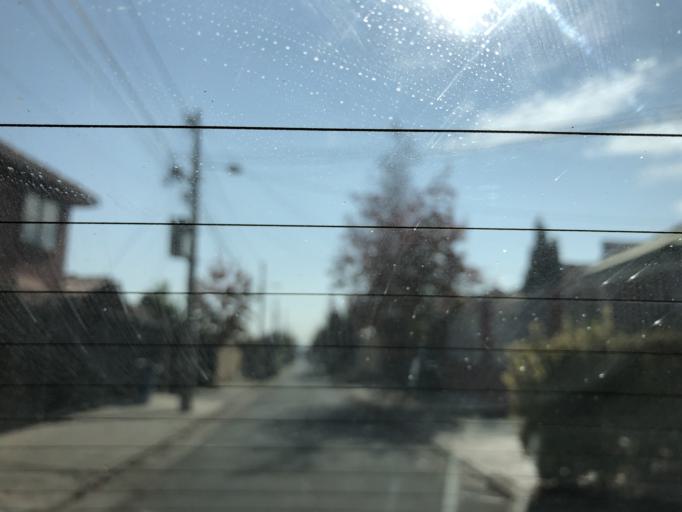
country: CL
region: Santiago Metropolitan
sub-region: Provincia de Cordillera
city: Puente Alto
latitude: -33.5725
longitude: -70.5461
